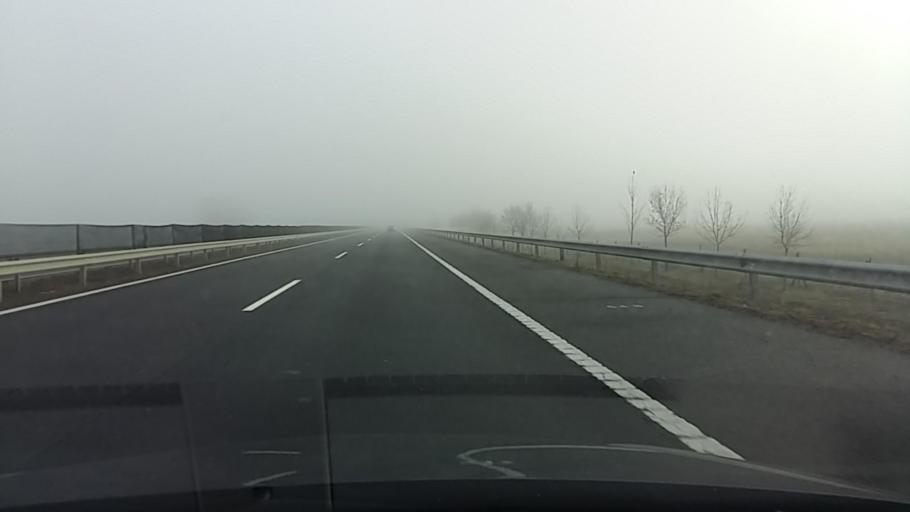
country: HU
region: Borsod-Abauj-Zemplen
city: Hejobaba
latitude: 47.8827
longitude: 20.8856
